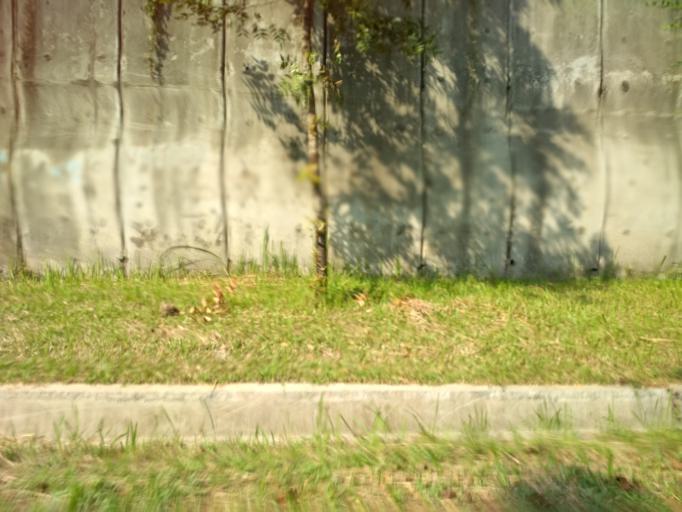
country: ID
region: West Java
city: Ciampea
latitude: -6.5563
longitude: 106.7203
